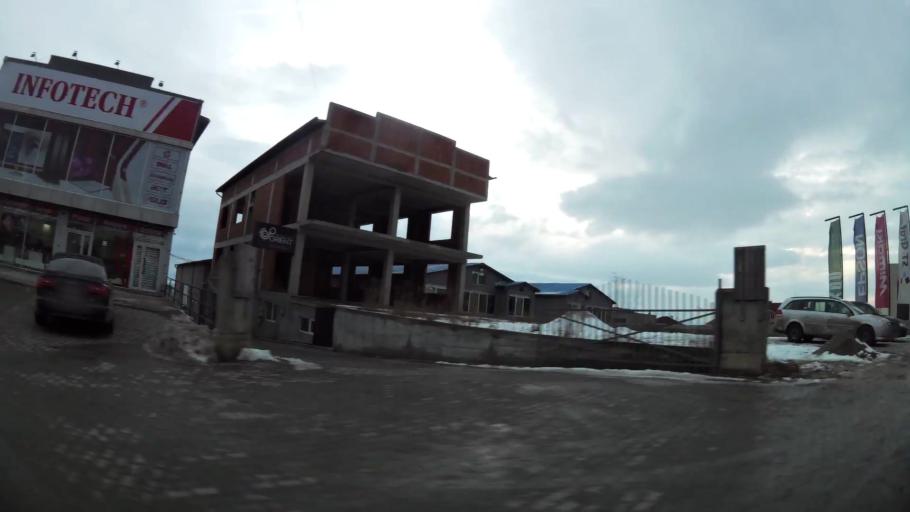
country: XK
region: Pristina
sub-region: Komuna e Prishtines
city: Pristina
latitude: 42.6206
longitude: 21.1641
